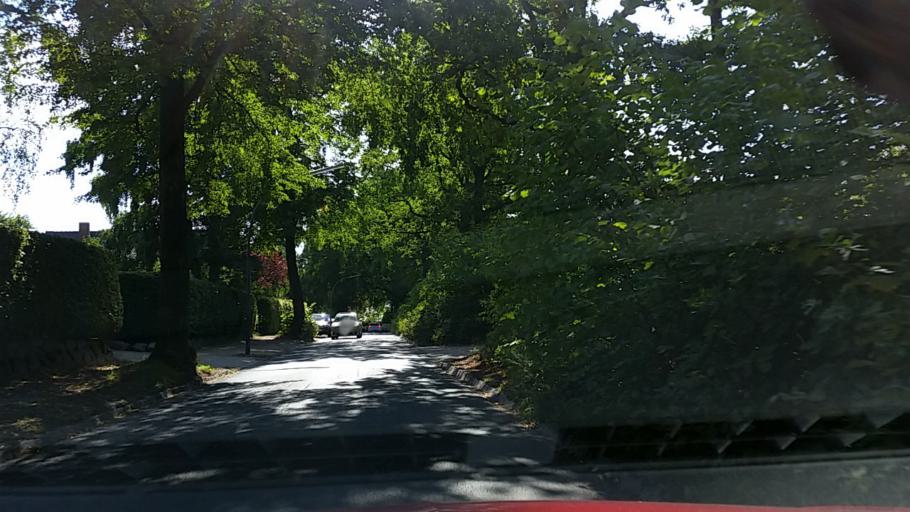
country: DE
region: Hamburg
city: Bergstedt
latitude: 53.6492
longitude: 10.1766
